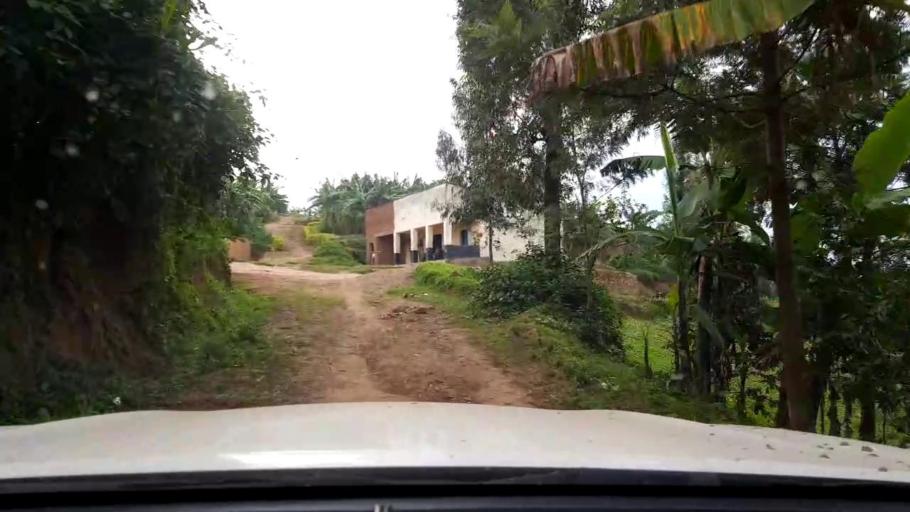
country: RW
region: Western Province
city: Kibuye
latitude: -2.0017
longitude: 29.3702
